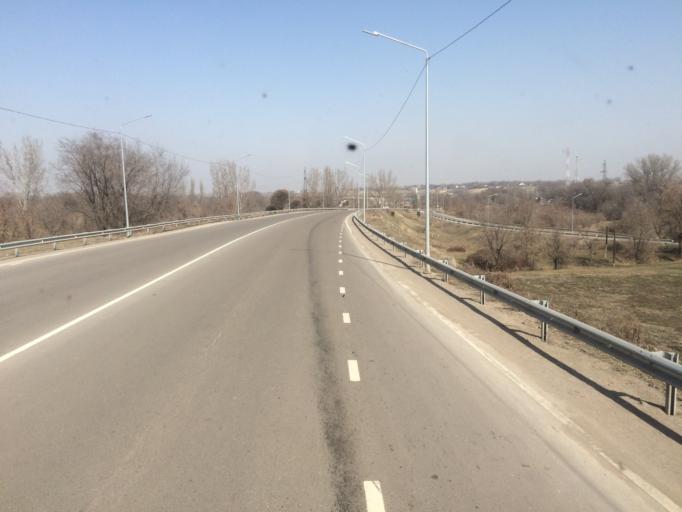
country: KZ
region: Almaty Oblysy
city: Burunday
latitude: 43.2190
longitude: 76.6488
